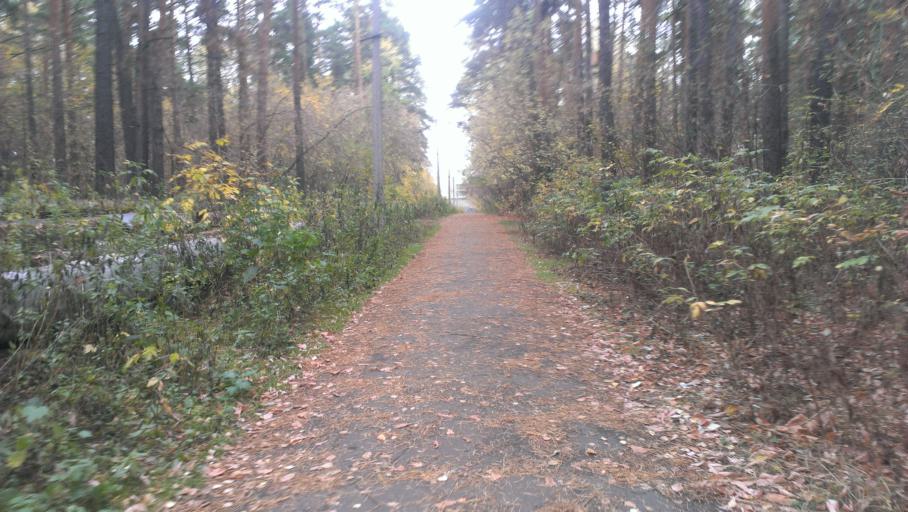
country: RU
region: Altai Krai
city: Yuzhnyy
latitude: 53.2599
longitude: 83.6889
